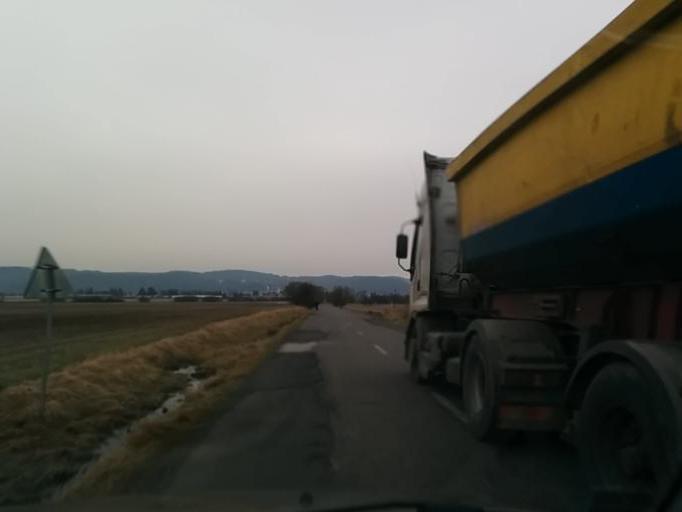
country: SK
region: Banskobystricky
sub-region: Okres Banska Bystrica
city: Zvolen
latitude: 48.6274
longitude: 19.1223
